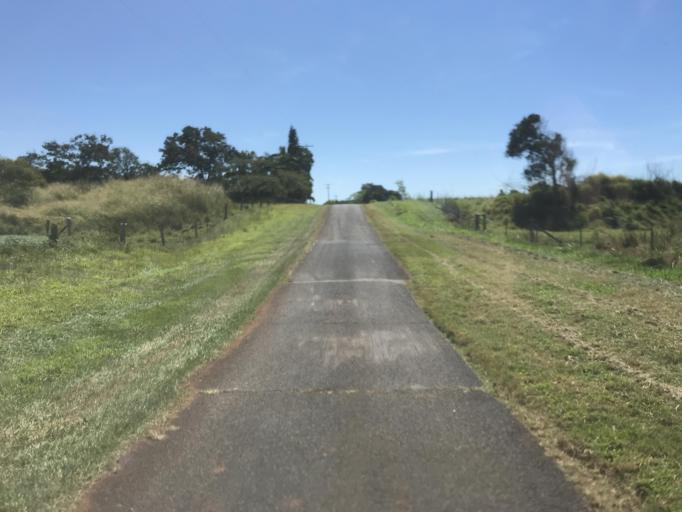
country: AU
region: Queensland
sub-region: Tablelands
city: Atherton
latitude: -17.2804
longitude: 145.5441
